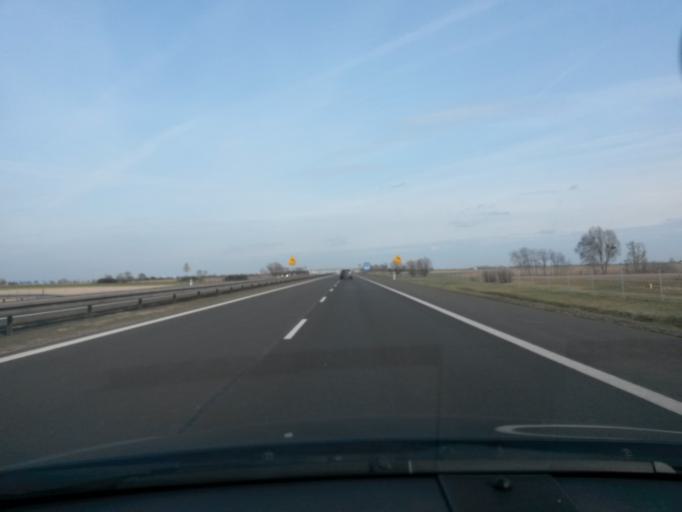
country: PL
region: Greater Poland Voivodeship
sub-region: Powiat slupecki
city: Ladek
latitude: 52.2148
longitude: 17.9765
